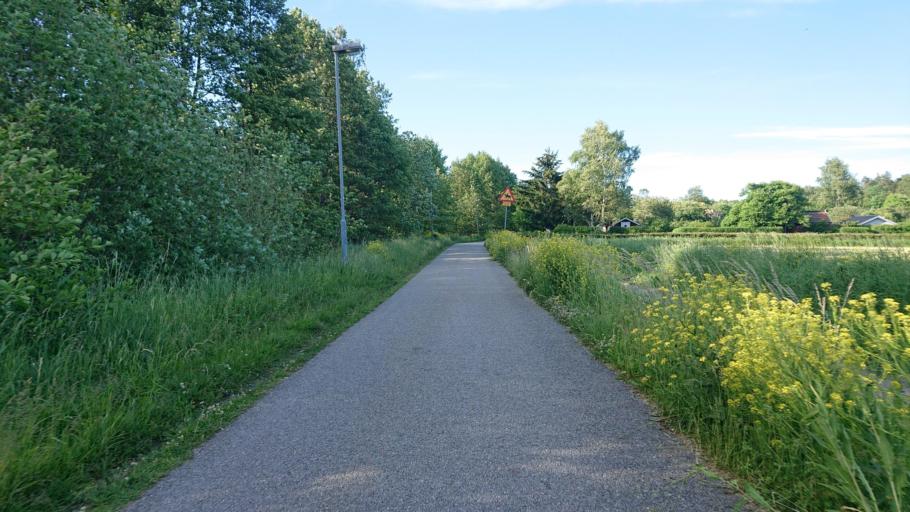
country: SE
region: Stockholm
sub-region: Osterakers Kommun
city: Akersberga
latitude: 59.4961
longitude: 18.2913
